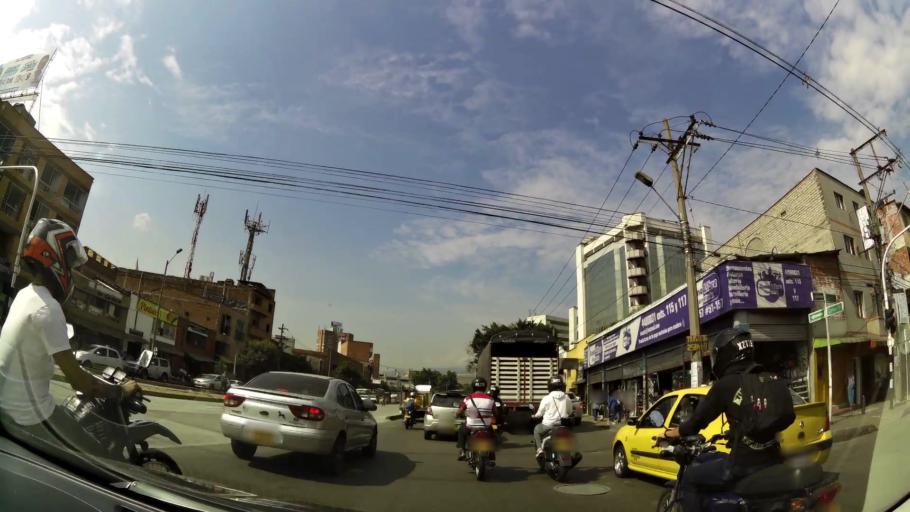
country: CO
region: Antioquia
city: Medellin
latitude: 6.2562
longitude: -75.5732
